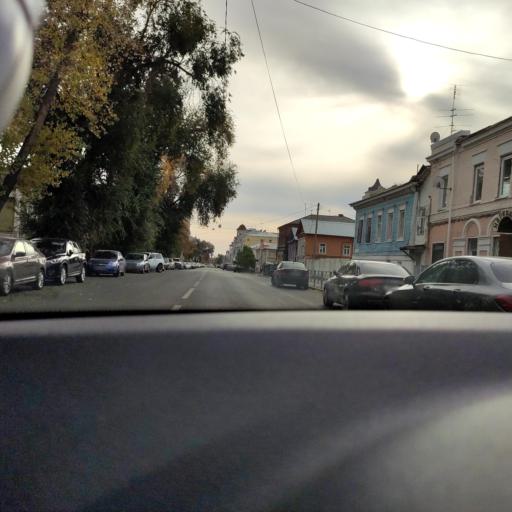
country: RU
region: Samara
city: Samara
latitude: 53.1908
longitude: 50.0990
